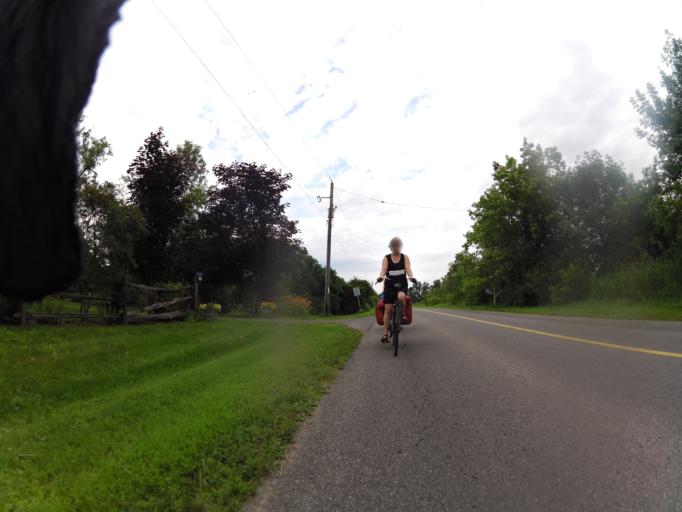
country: CA
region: Ontario
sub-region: Lanark County
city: Smiths Falls
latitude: 44.9929
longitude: -75.7639
